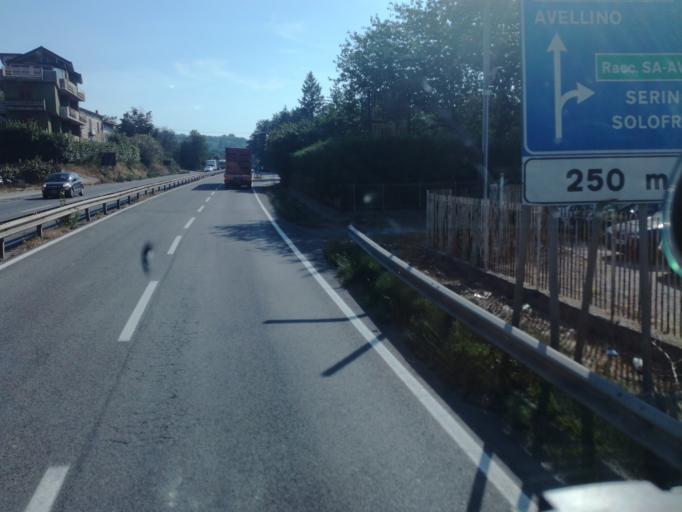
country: IT
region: Campania
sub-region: Provincia di Avellino
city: Atripalda
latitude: 40.9154
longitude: 14.8247
